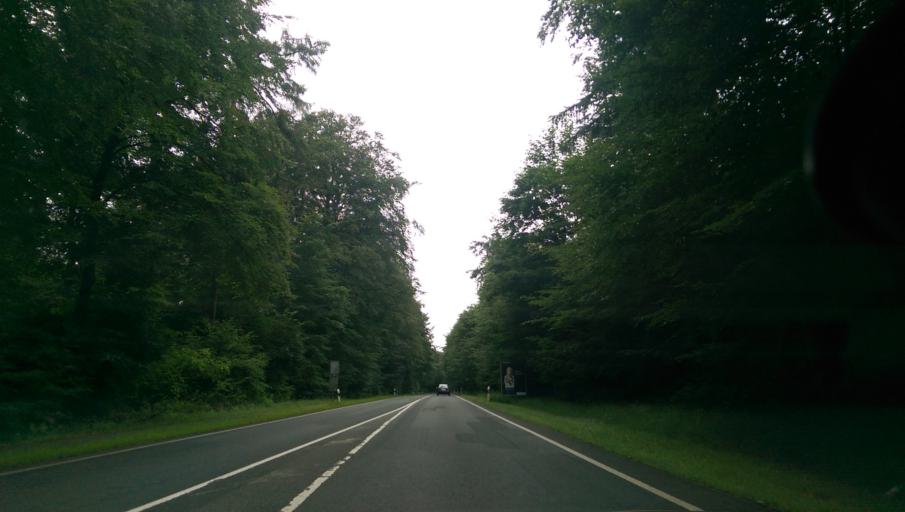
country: DE
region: Lower Saxony
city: Botersen
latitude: 53.1405
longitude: 9.3521
